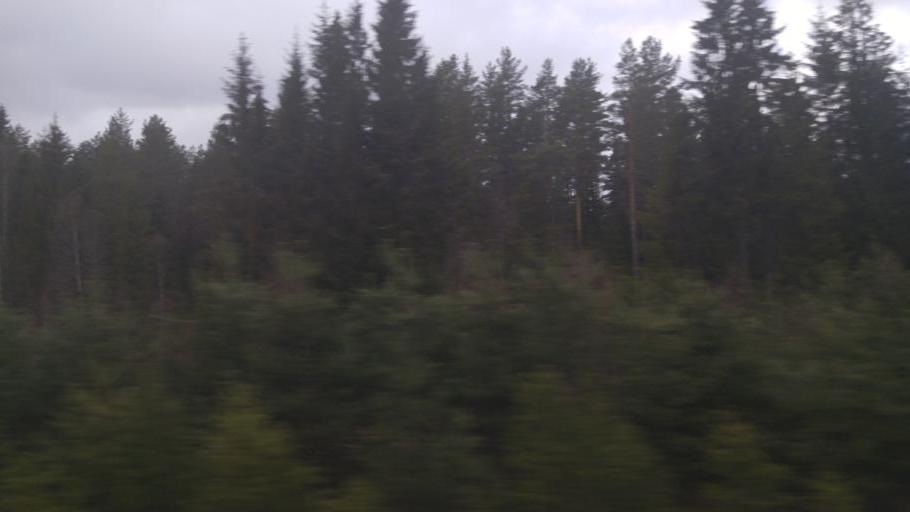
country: NO
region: Akershus
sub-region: Eidsvoll
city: Raholt
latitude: 60.2425
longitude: 11.1158
